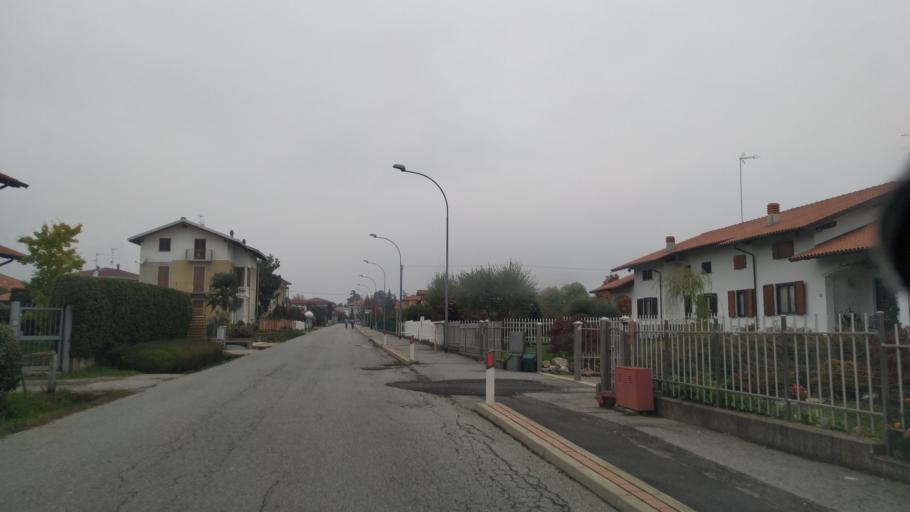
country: IT
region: Piedmont
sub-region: Provincia di Biella
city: Lessona
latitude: 45.5788
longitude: 8.2011
